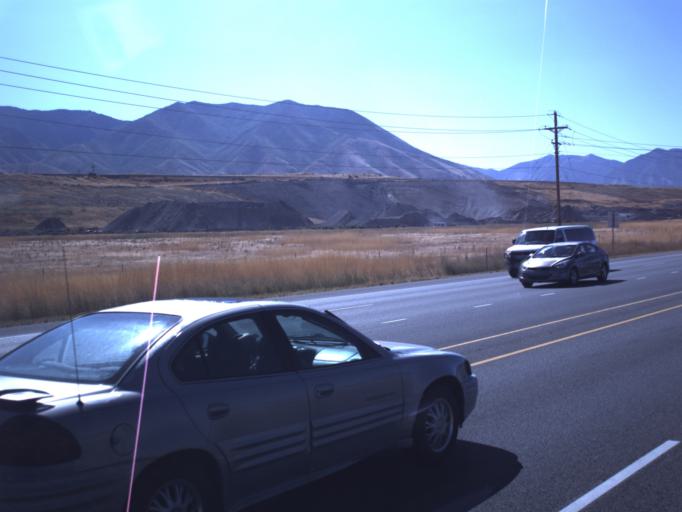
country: US
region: Utah
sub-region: Tooele County
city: Stansbury park
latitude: 40.6490
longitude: -112.2887
